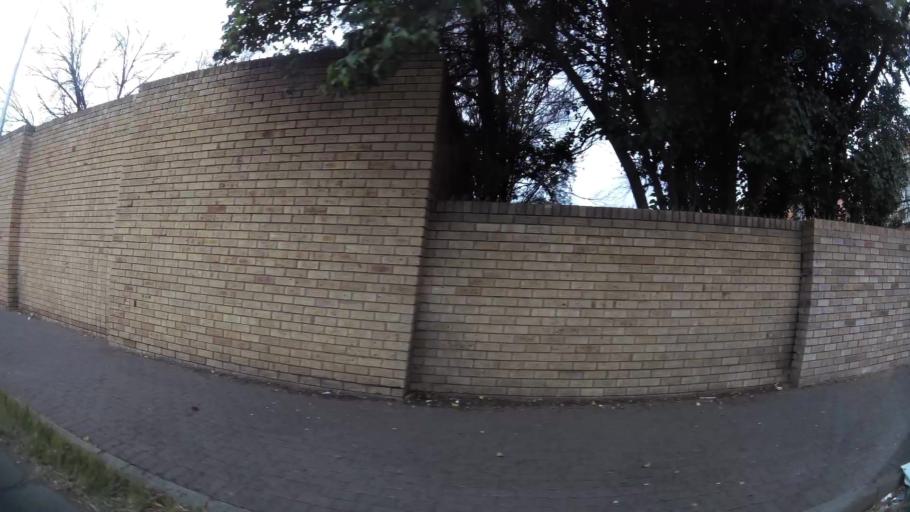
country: ZA
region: Orange Free State
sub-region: Mangaung Metropolitan Municipality
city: Bloemfontein
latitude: -29.1200
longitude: 26.2127
